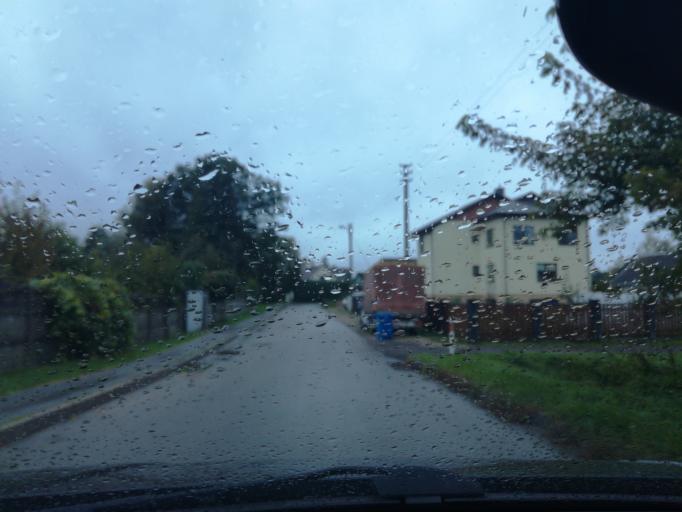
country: LT
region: Alytaus apskritis
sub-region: Alytus
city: Alytus
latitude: 54.4038
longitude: 24.0564
